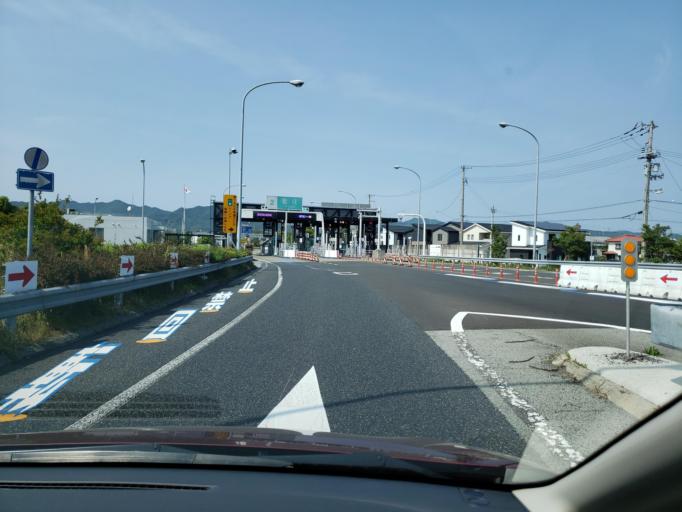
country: JP
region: Tokushima
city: Ishii
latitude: 34.1183
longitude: 134.4794
